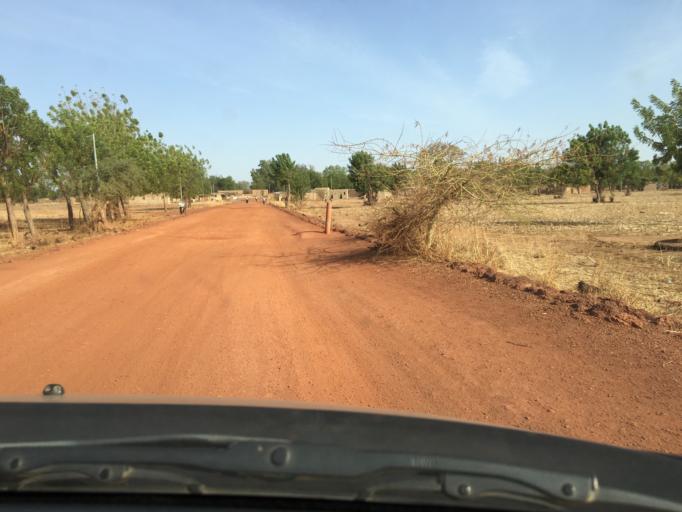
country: BF
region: Plateau-Central
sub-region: Province du Kourweogo
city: Bousse
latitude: 12.5733
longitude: -1.9293
